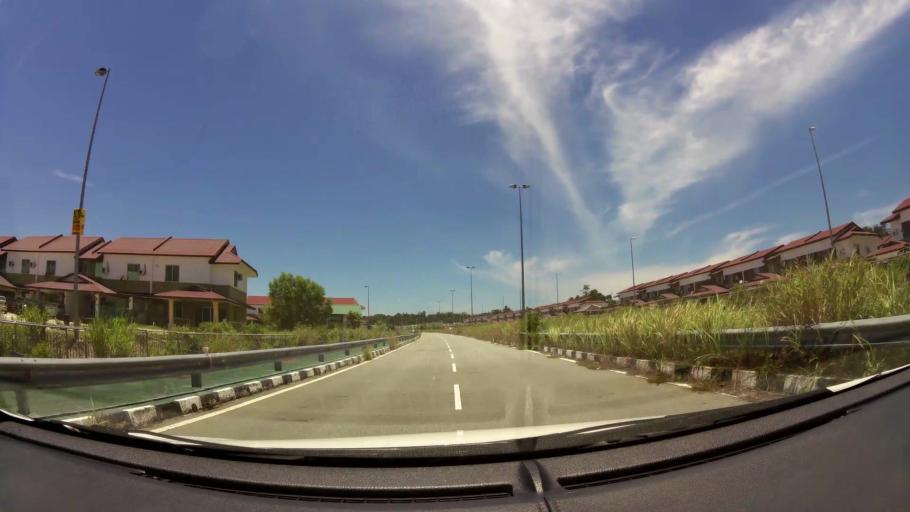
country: BN
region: Brunei and Muara
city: Bandar Seri Begawan
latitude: 5.0108
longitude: 115.0133
